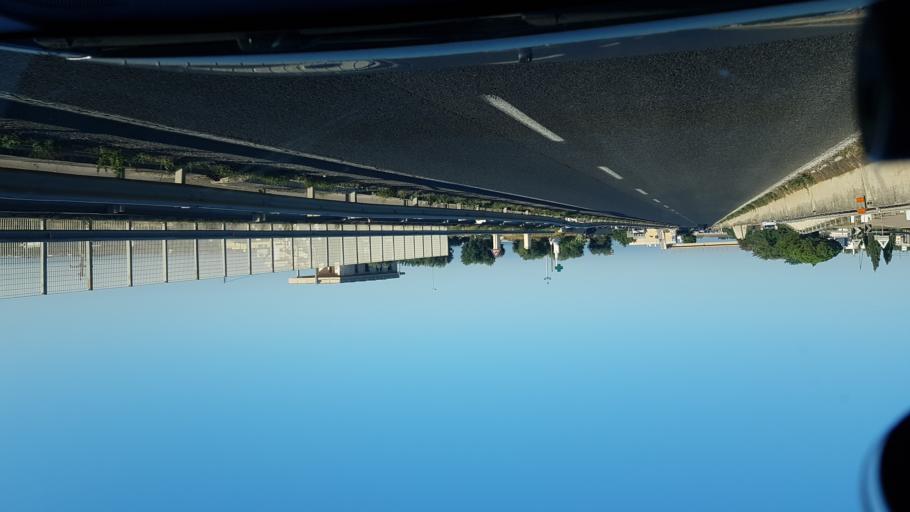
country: IT
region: Apulia
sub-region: Provincia di Brindisi
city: Fasano
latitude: 40.8881
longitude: 17.3343
